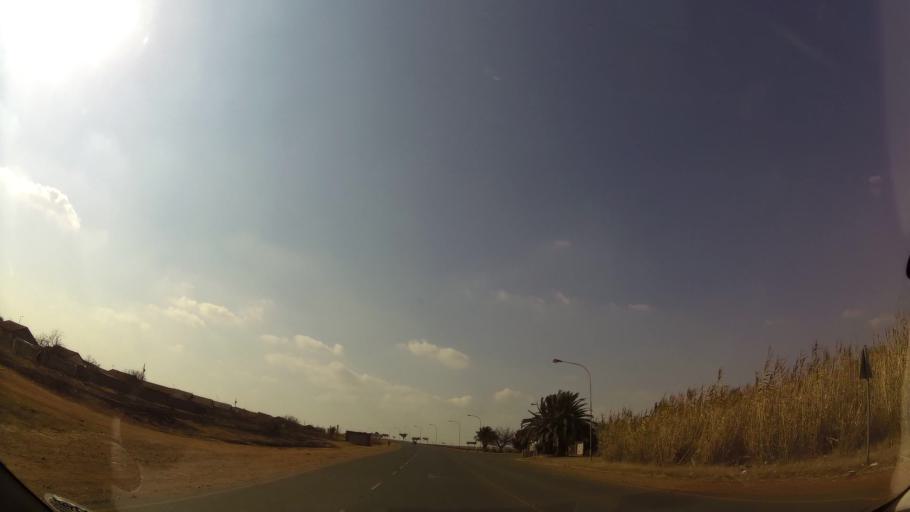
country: ZA
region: Gauteng
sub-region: Ekurhuleni Metropolitan Municipality
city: Springs
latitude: -26.1356
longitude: 28.4678
